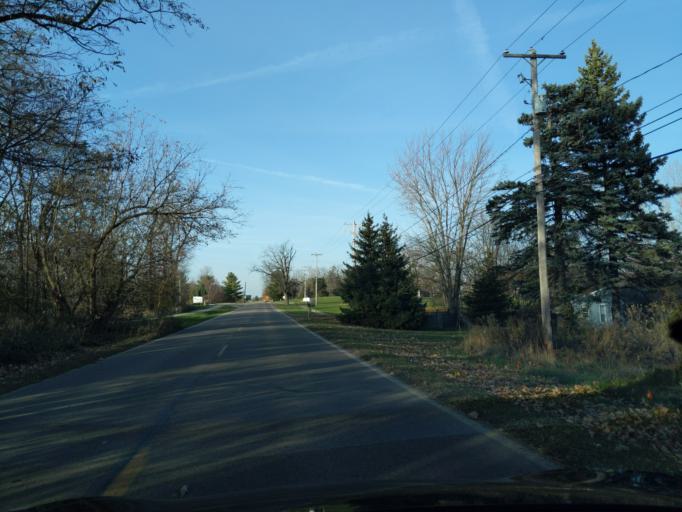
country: US
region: Michigan
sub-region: Ingham County
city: East Lansing
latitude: 42.7674
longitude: -84.5084
